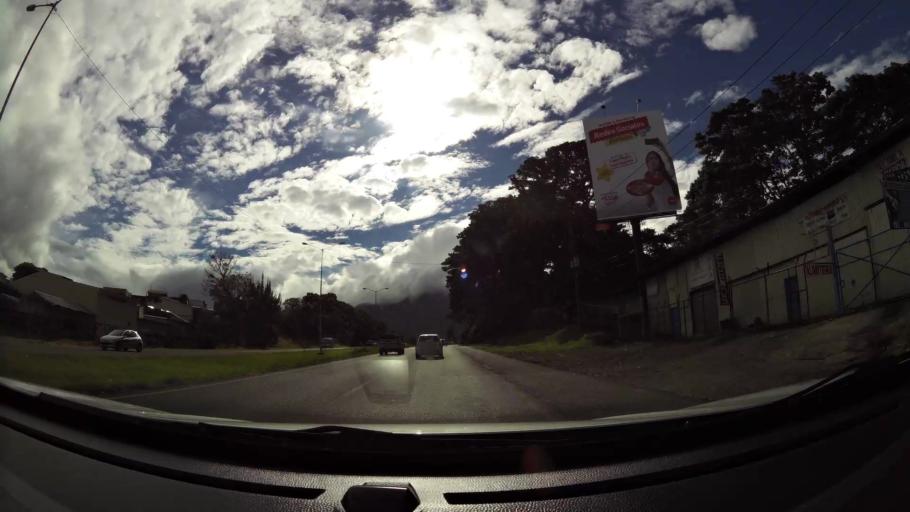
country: CR
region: Cartago
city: San Diego
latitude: 9.9041
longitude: -84.0101
